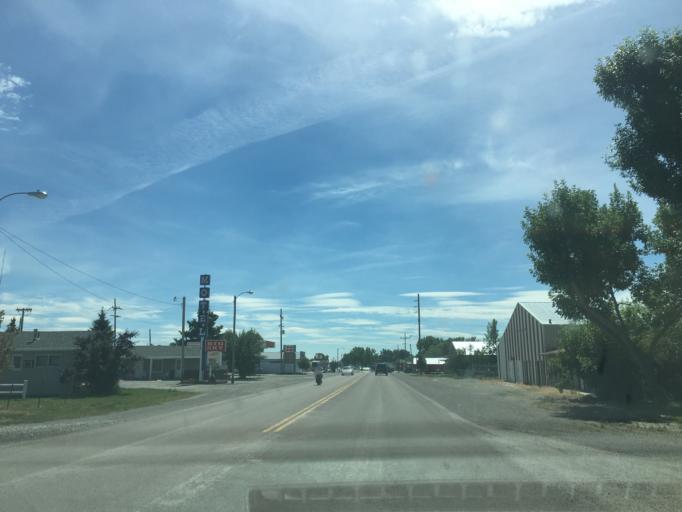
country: US
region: Montana
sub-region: Teton County
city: Choteau
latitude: 47.8092
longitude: -112.1810
